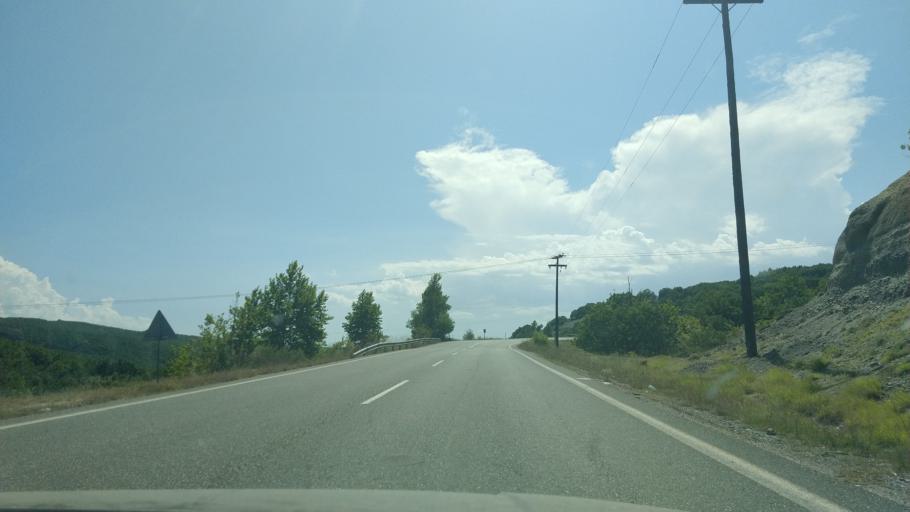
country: GR
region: West Macedonia
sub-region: Nomos Grevenon
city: Grevena
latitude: 40.0510
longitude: 21.4780
